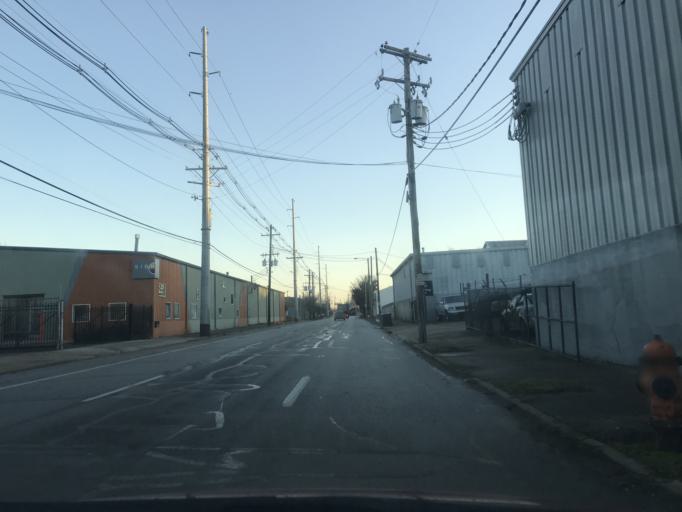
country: US
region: Indiana
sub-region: Clark County
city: Jeffersonville
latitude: 38.2584
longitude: -85.7187
